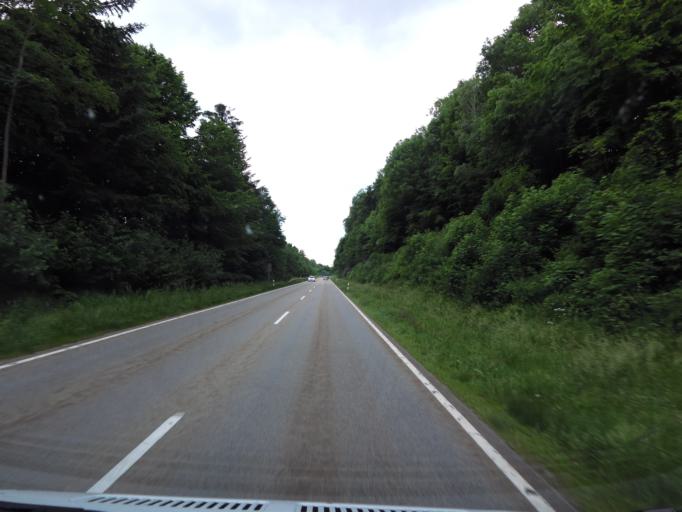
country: DE
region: Bavaria
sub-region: Lower Bavaria
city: Witzmannsberg
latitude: 48.6900
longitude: 13.4147
